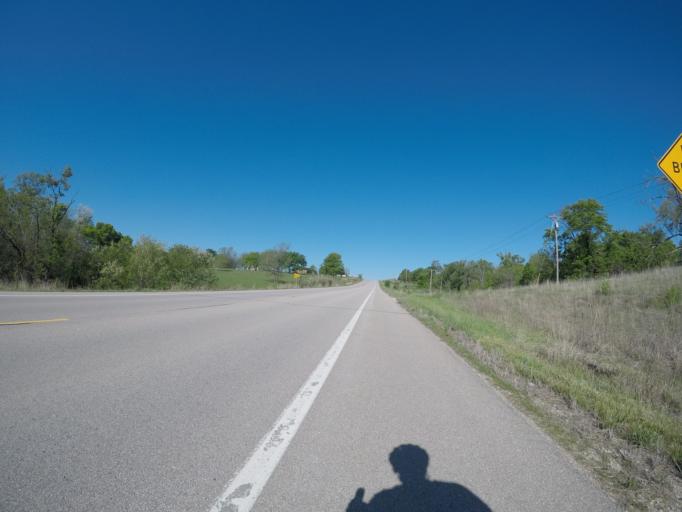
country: US
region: Kansas
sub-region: Douglas County
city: Lawrence
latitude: 38.9714
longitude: -95.4213
